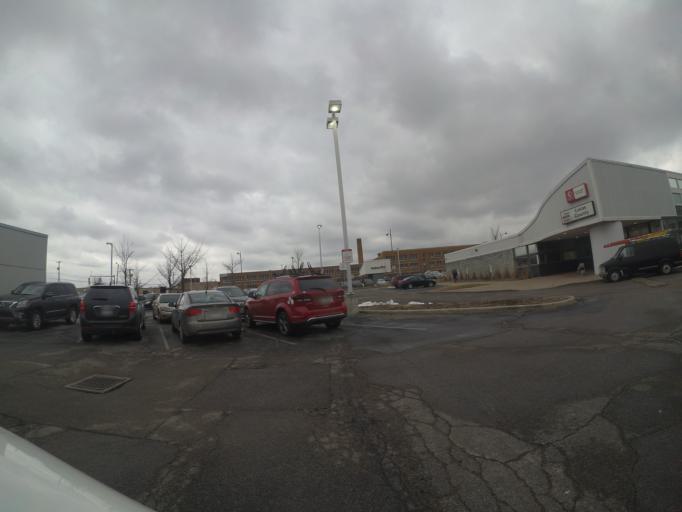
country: US
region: Ohio
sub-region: Lucas County
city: Toledo
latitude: 41.6519
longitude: -83.5463
